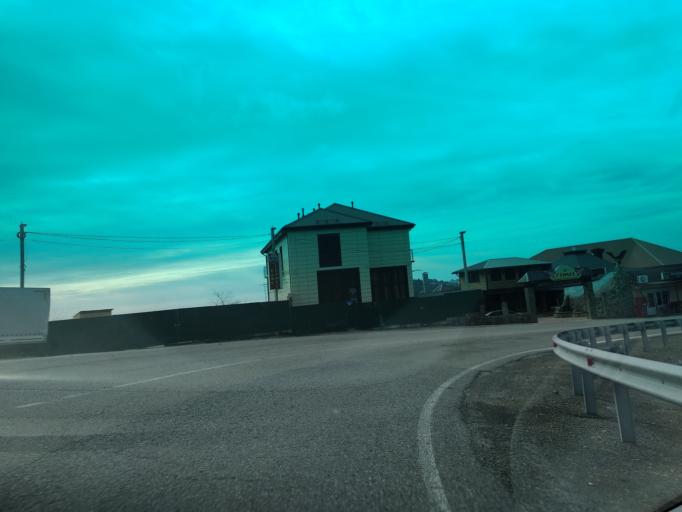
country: RU
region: Krasnodarskiy
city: Tuapse
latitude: 44.0872
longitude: 39.1246
